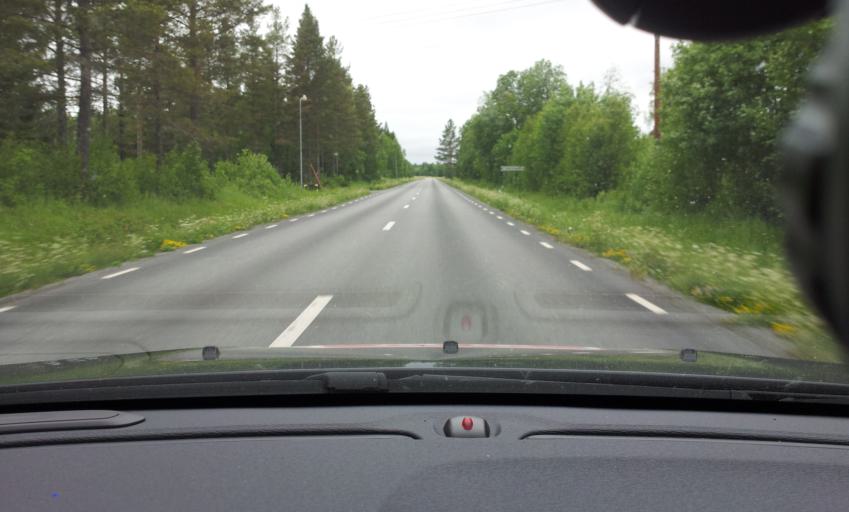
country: SE
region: Jaemtland
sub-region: Bergs Kommun
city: Hoverberg
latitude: 62.9863
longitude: 14.4387
